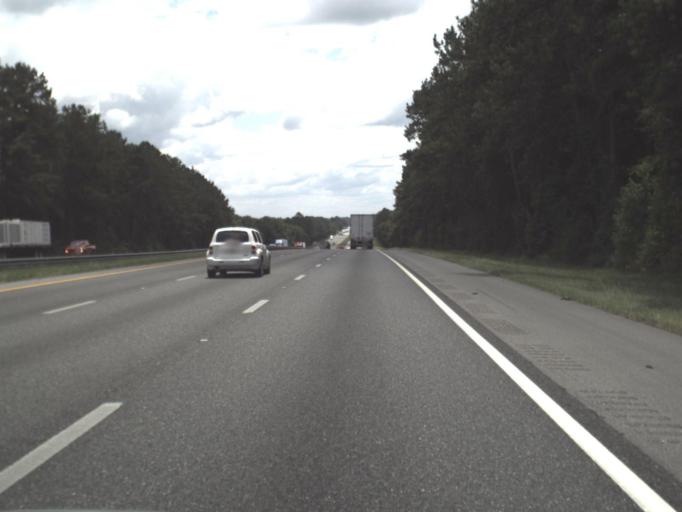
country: US
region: Florida
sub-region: Alachua County
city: High Springs
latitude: 29.9380
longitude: -82.5639
